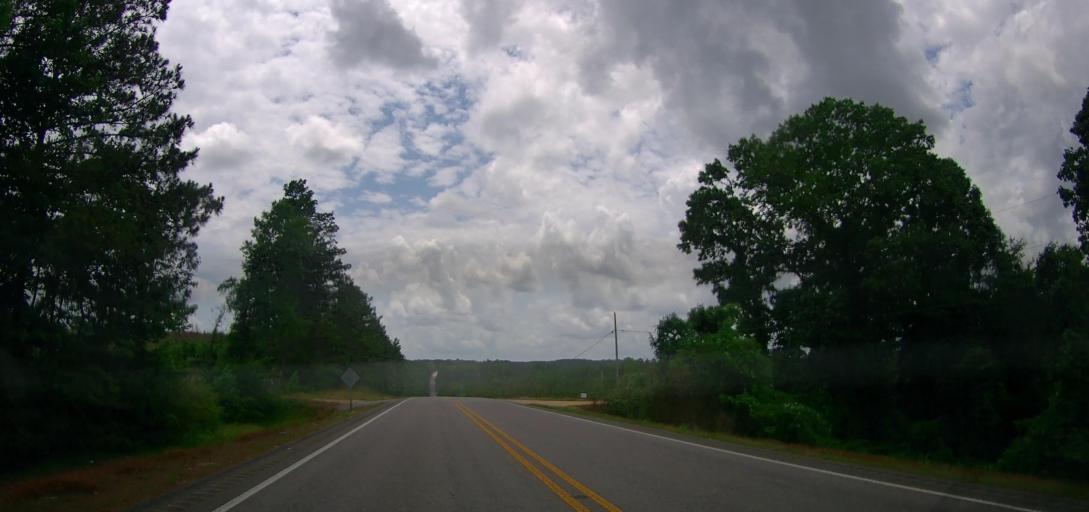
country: US
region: Alabama
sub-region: Marion County
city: Hamilton
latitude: 34.1338
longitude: -88.0217
